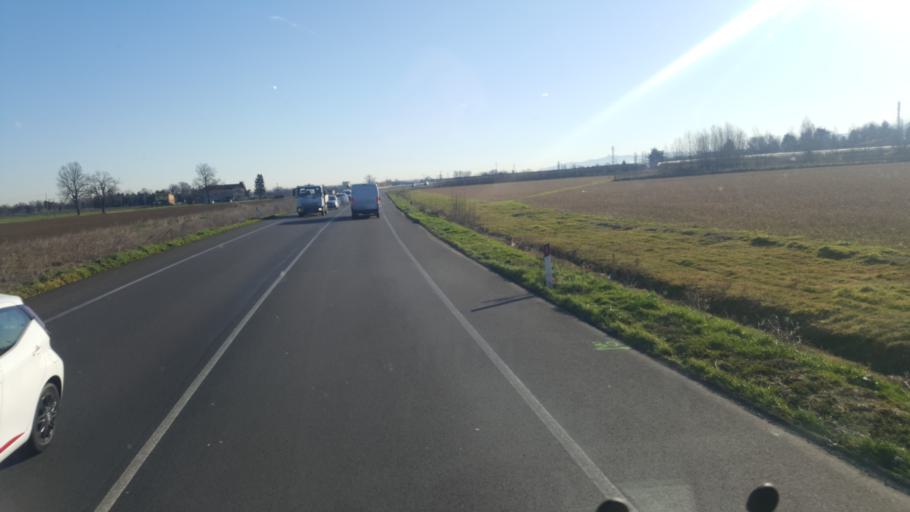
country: IT
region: Emilia-Romagna
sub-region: Provincia di Bologna
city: Crespellano
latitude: 44.5224
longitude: 11.1283
